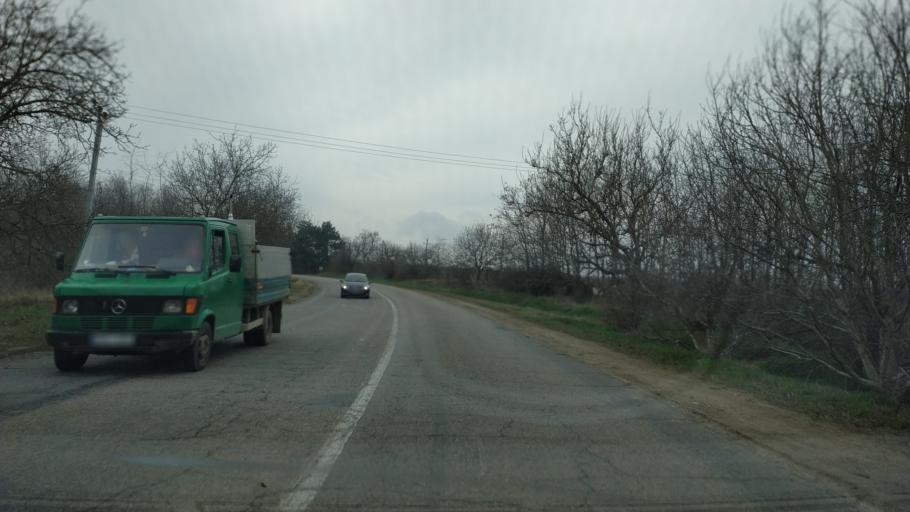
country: MD
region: Cahul
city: Cahul
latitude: 45.9543
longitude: 28.3453
